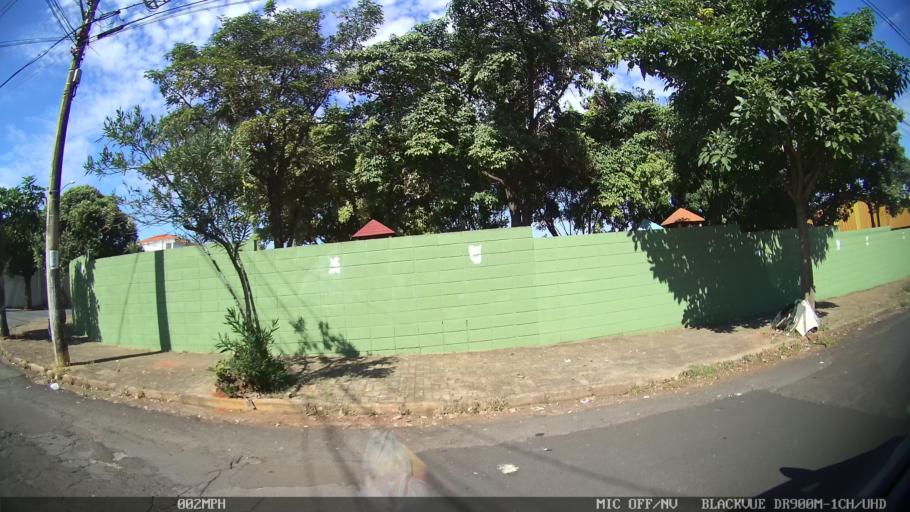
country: BR
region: Sao Paulo
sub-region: Santa Barbara D'Oeste
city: Santa Barbara d'Oeste
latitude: -22.7385
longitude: -47.3824
